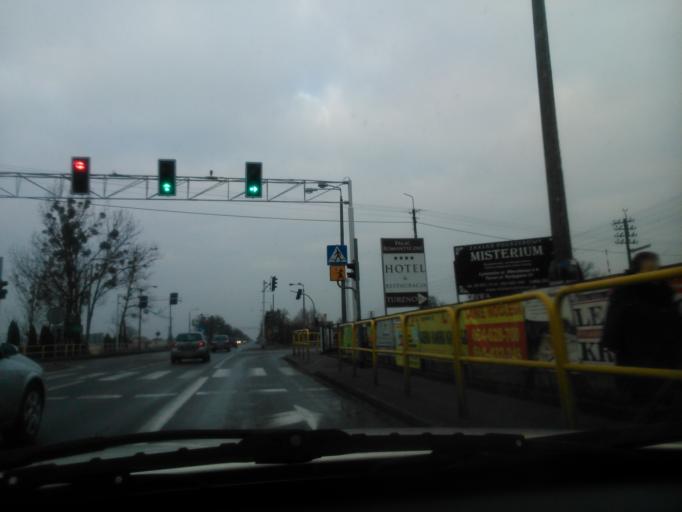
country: PL
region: Kujawsko-Pomorskie
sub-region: Powiat torunski
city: Lysomice
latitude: 53.0859
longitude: 18.6199
